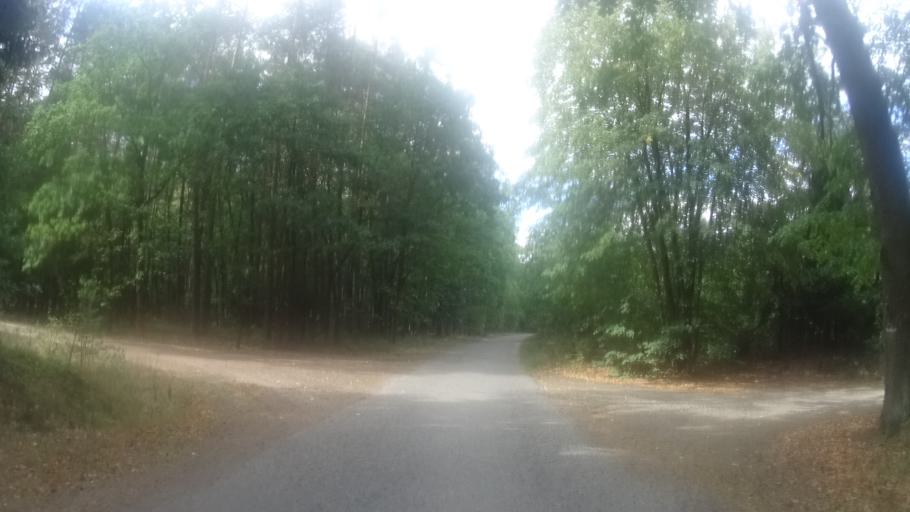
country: CZ
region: Pardubicky
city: Horni Jeleni
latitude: 50.0525
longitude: 16.1533
